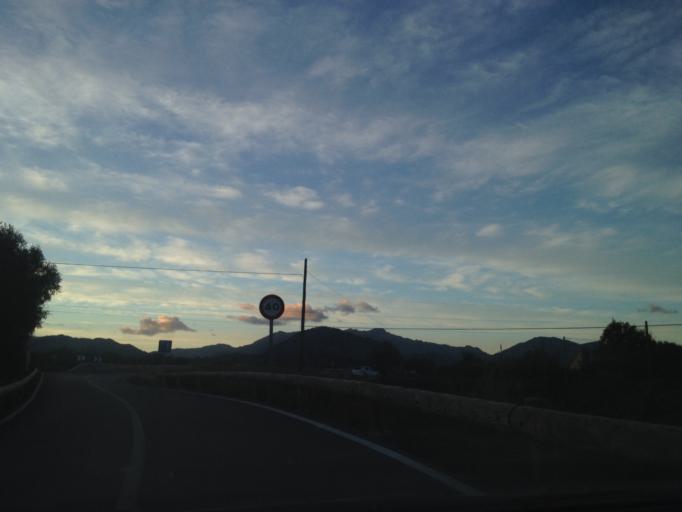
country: ES
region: Balearic Islands
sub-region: Illes Balears
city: Pollenca
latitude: 39.8529
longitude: 3.0611
